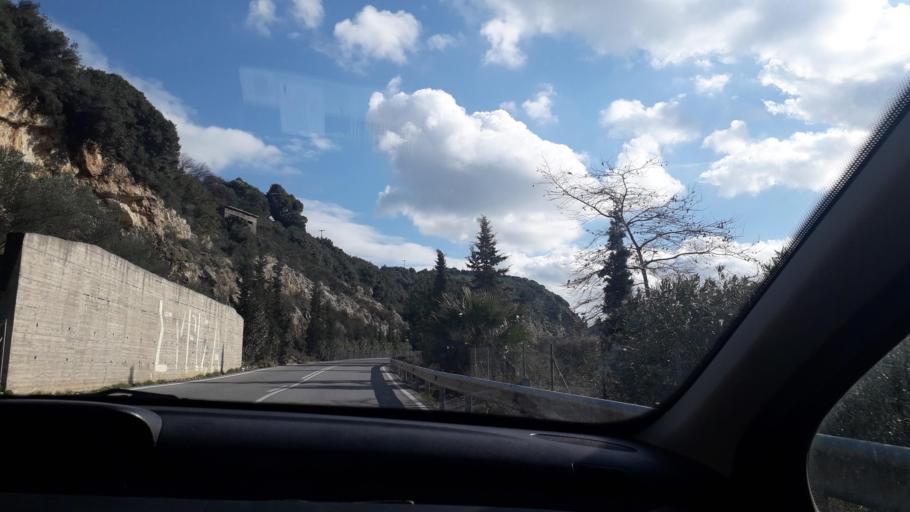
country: GR
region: Crete
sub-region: Nomos Rethymnis
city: Rethymno
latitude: 35.3334
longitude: 24.5270
